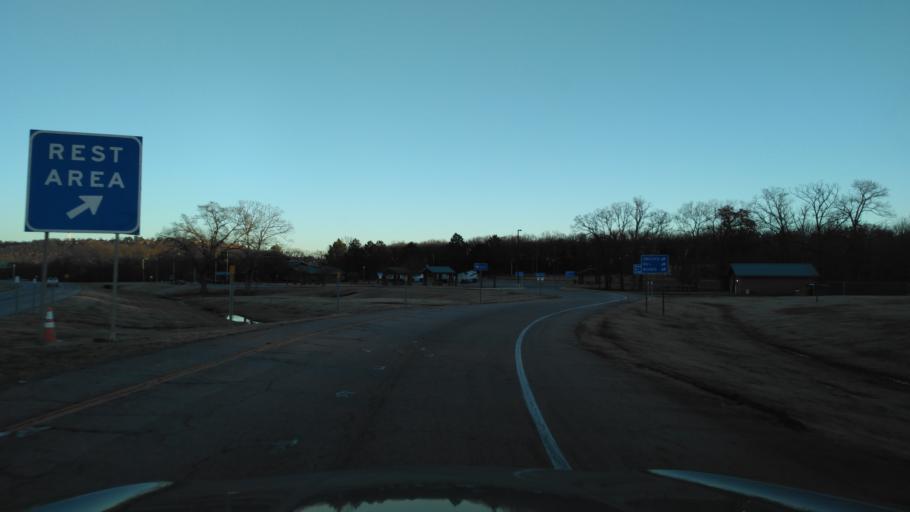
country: US
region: Arkansas
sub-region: Crawford County
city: Van Buren
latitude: 35.4598
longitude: -94.4009
